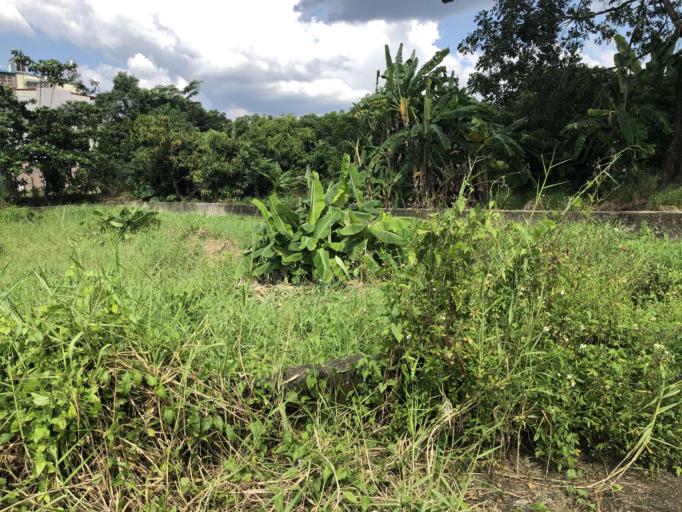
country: TW
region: Taiwan
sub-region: Pingtung
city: Pingtung
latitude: 22.8988
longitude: 120.5497
